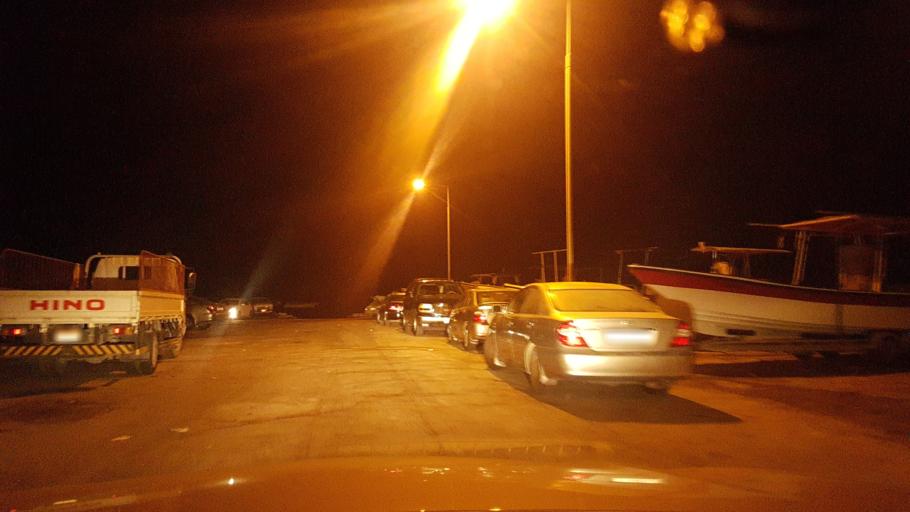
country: BH
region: Central Governorate
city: Madinat Hamad
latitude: 26.0968
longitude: 50.4783
